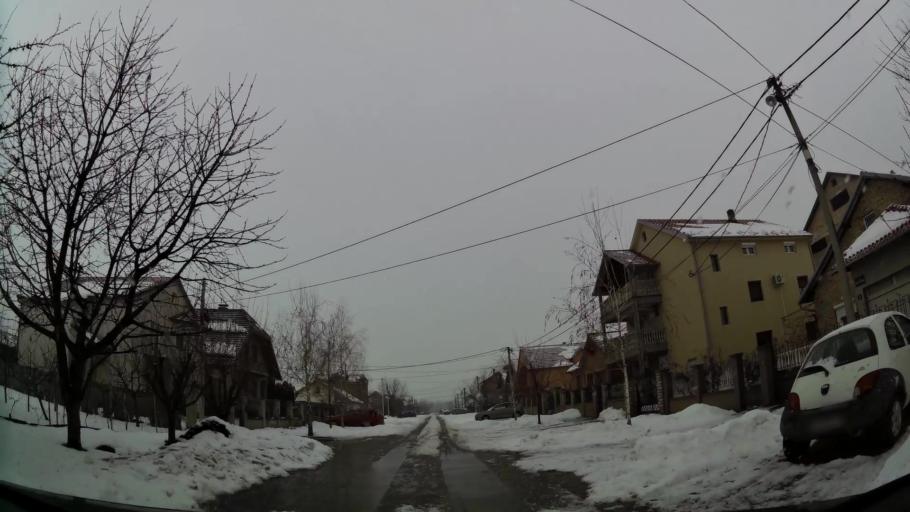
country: RS
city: Novi Banovci
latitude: 44.8781
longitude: 20.3195
